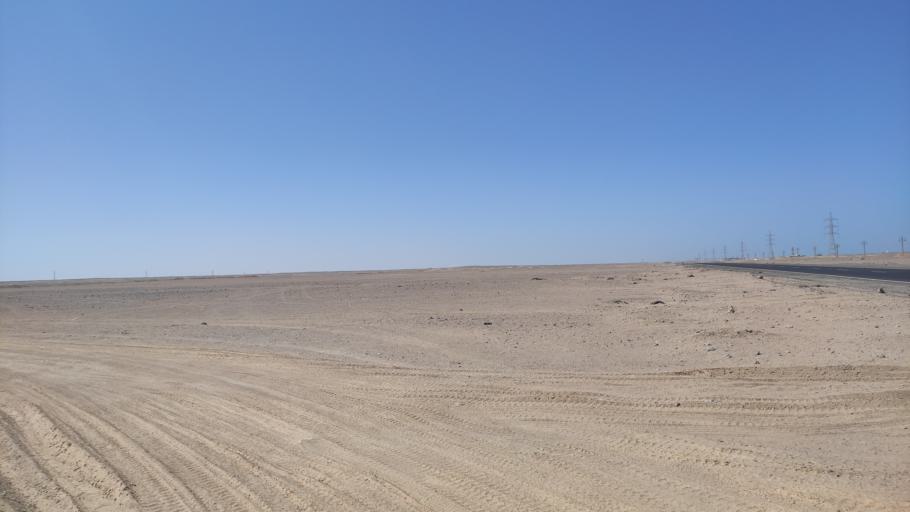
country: EG
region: Red Sea
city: Makadi Bay
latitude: 27.0332
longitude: 33.8348
